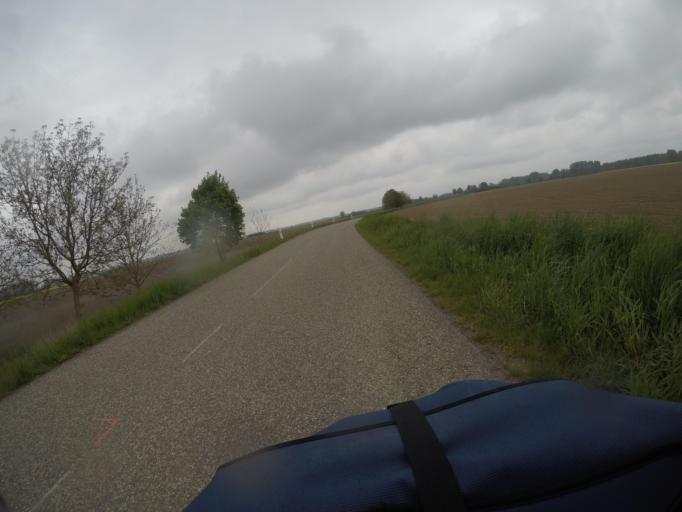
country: FR
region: Alsace
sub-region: Departement du Bas-Rhin
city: Roppenheim
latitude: 48.8238
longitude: 8.0565
